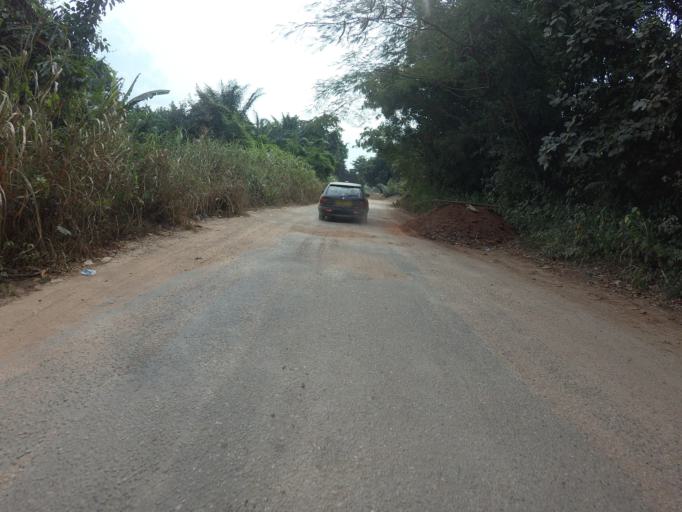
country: GH
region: Volta
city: Ho
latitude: 6.6831
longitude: 0.3371
